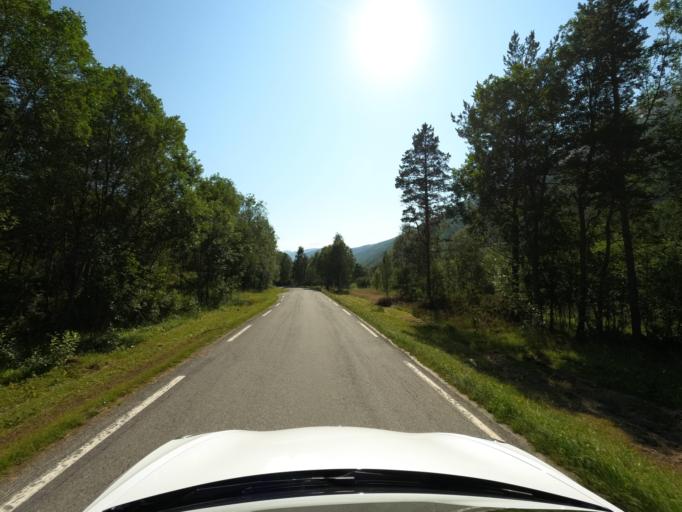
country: NO
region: Nordland
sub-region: Narvik
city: Narvik
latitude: 68.1894
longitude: 17.5520
